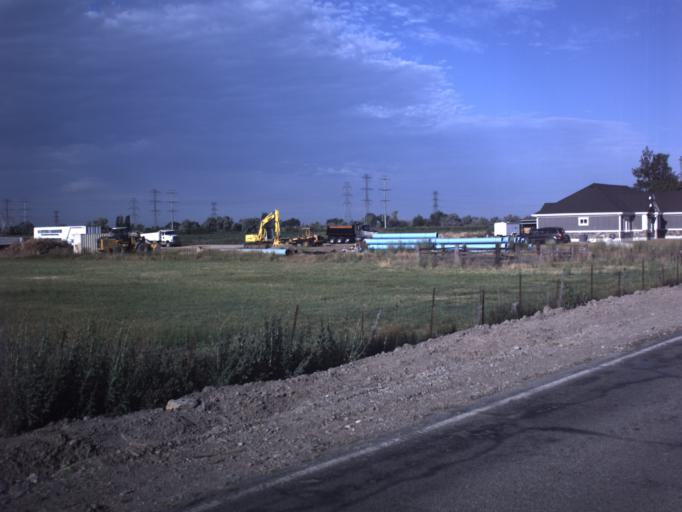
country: US
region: Utah
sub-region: Weber County
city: Farr West
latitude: 41.3050
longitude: -112.0497
